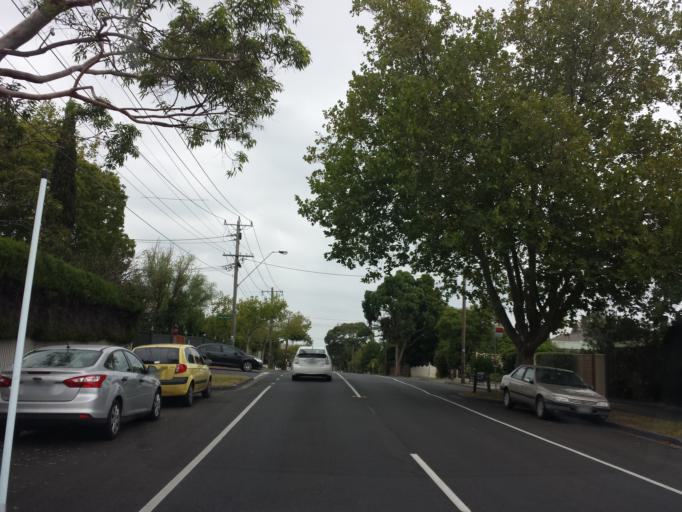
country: AU
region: Victoria
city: Glenferrie
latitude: -37.8332
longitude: 145.0430
